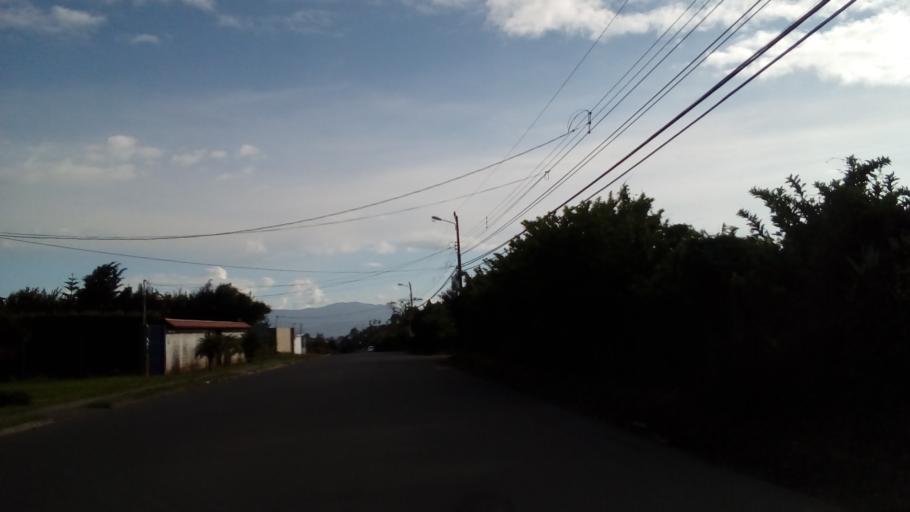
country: CR
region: Heredia
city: Angeles
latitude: 10.0033
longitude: -84.0524
